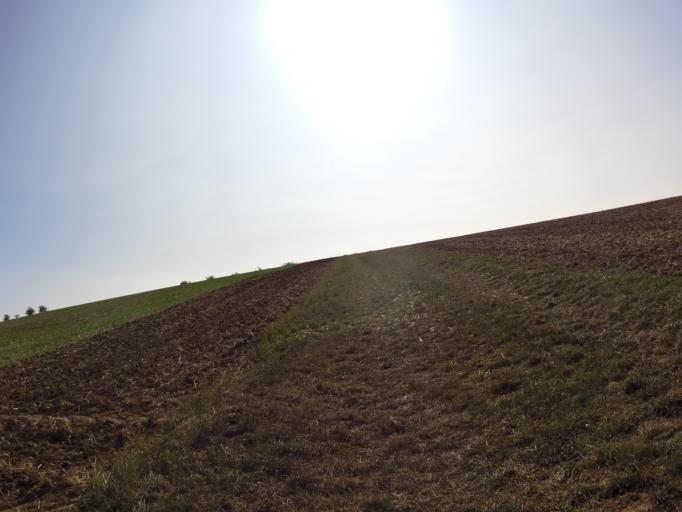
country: DE
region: Bavaria
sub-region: Regierungsbezirk Unterfranken
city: Hettstadt
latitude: 49.7826
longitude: 9.8195
